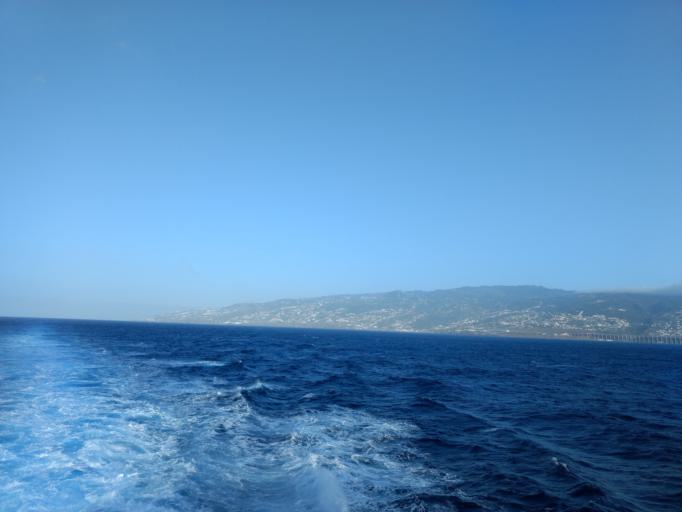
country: PT
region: Madeira
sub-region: Machico
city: Machico
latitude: 32.6817
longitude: -16.7187
